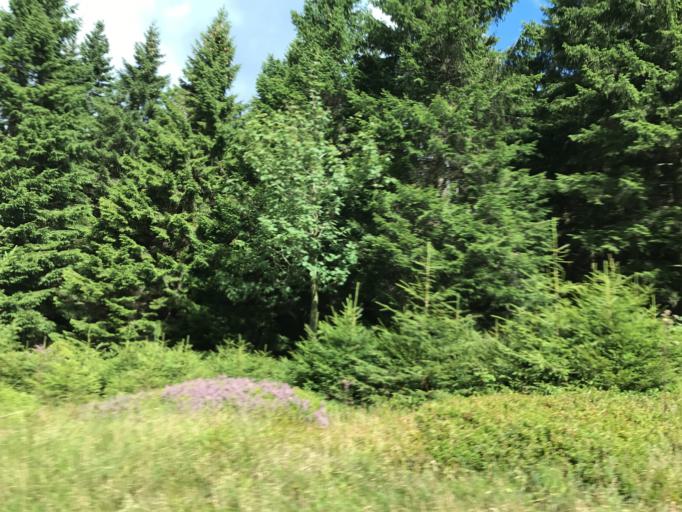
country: DE
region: Lower Saxony
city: Bad Harzburg
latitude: 51.8100
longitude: 10.5258
